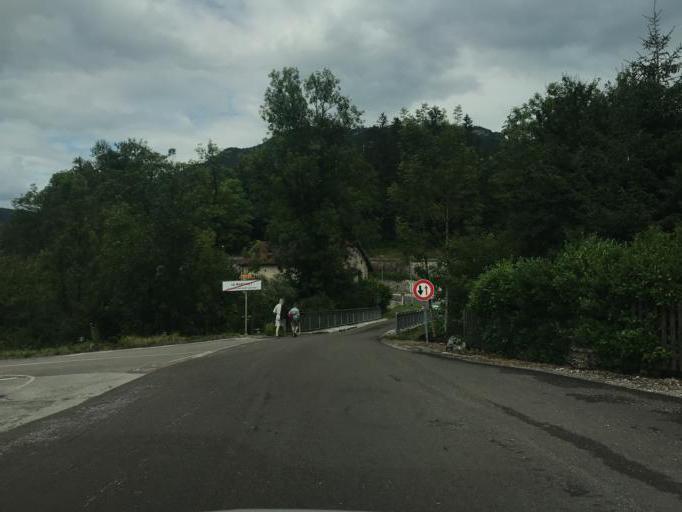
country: FR
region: Franche-Comte
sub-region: Departement du Jura
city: Saint-Claude
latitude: 46.3752
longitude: 5.8742
